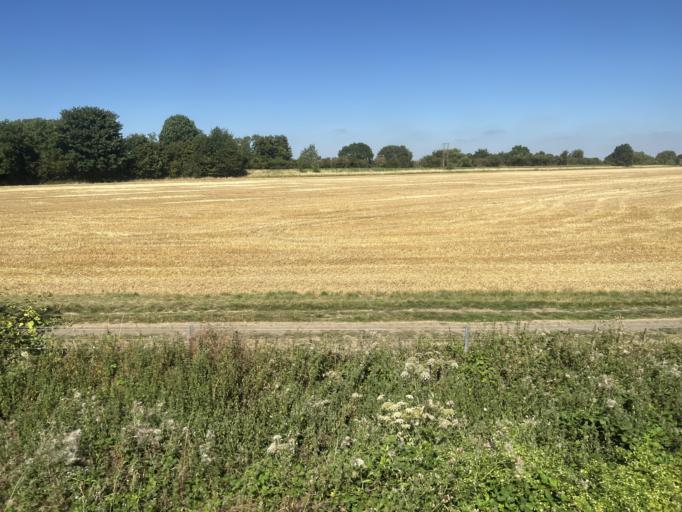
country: GB
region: England
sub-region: Lincolnshire
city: Boston
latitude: 52.9999
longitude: -0.0187
